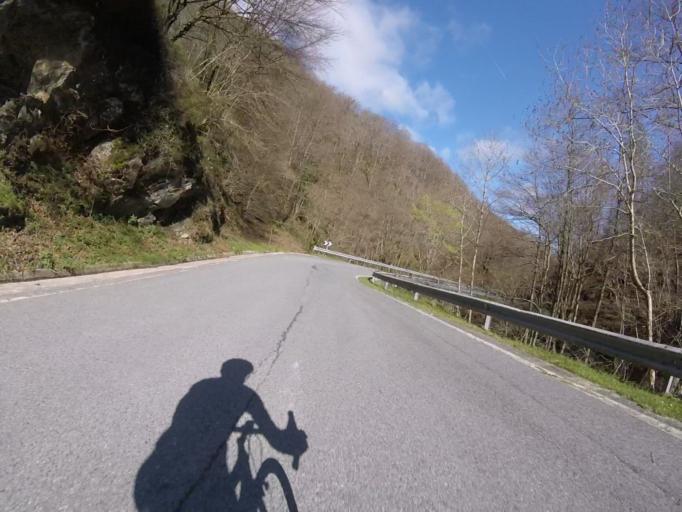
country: ES
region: Navarre
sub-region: Provincia de Navarra
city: Ezkurra
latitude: 43.0976
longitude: -1.8645
